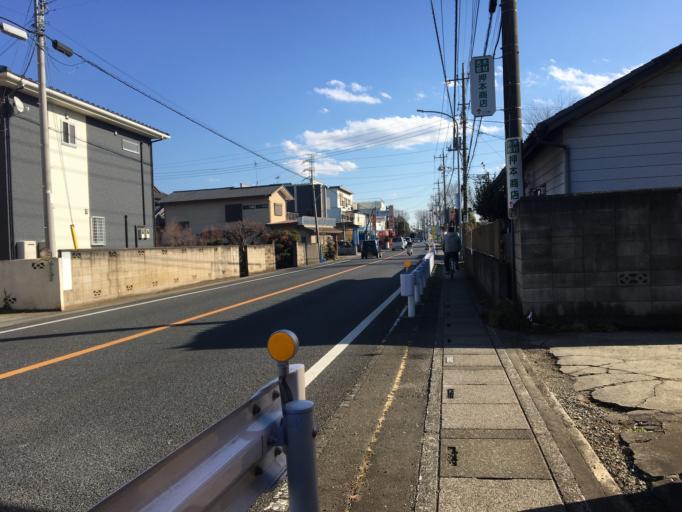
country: JP
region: Saitama
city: Oi
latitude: 35.8461
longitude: 139.5199
